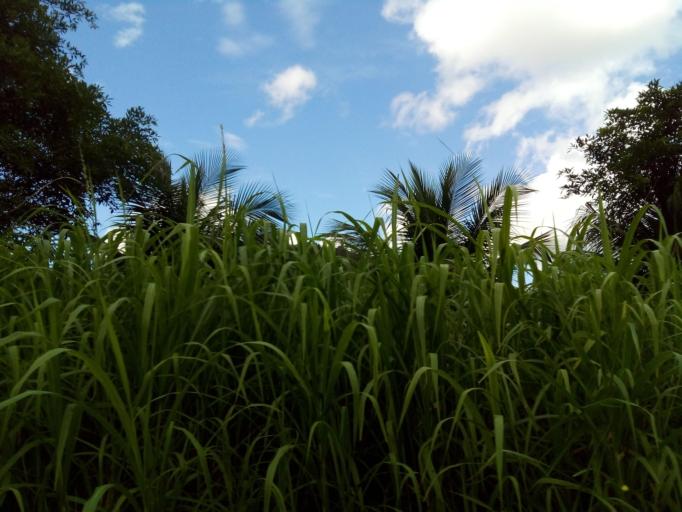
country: BR
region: Espirito Santo
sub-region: Ibiracu
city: Ibiracu
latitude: -19.8690
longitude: -40.3614
